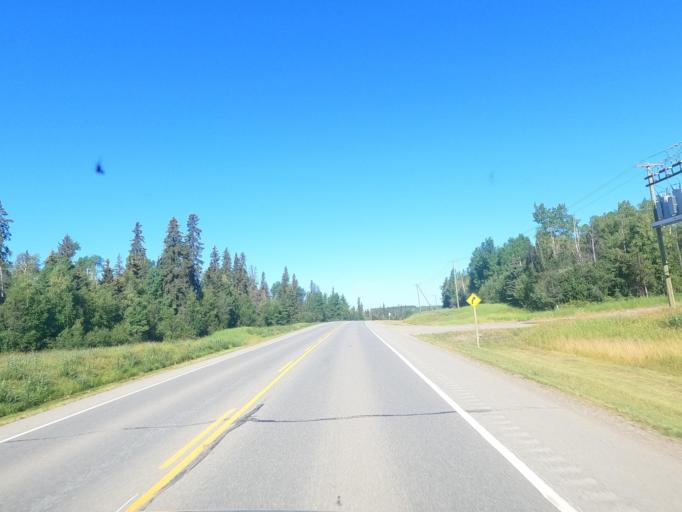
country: CA
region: British Columbia
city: Fort St. John
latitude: 56.5952
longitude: -121.4597
